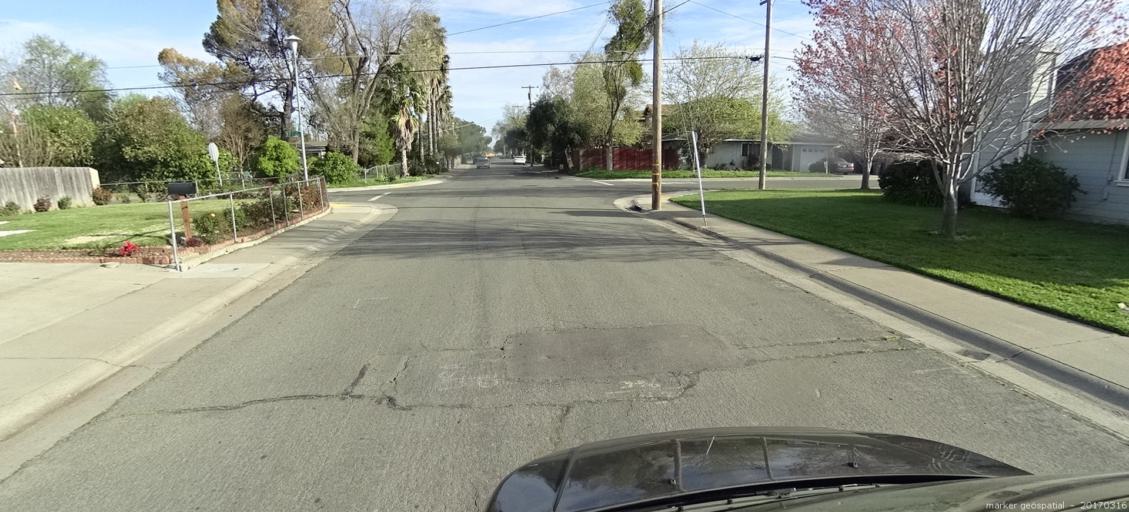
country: US
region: California
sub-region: Sacramento County
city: Parkway
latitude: 38.4991
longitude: -121.4774
